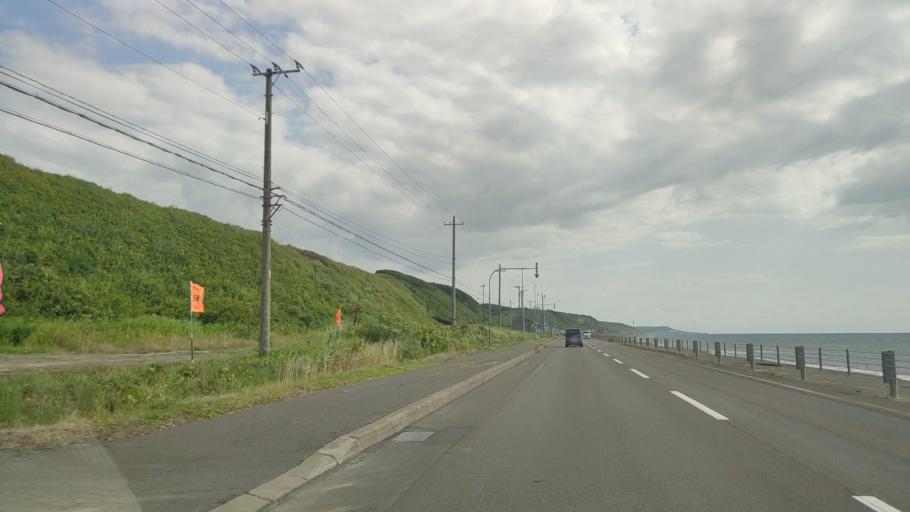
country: JP
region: Hokkaido
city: Rumoi
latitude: 44.2104
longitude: 141.6566
